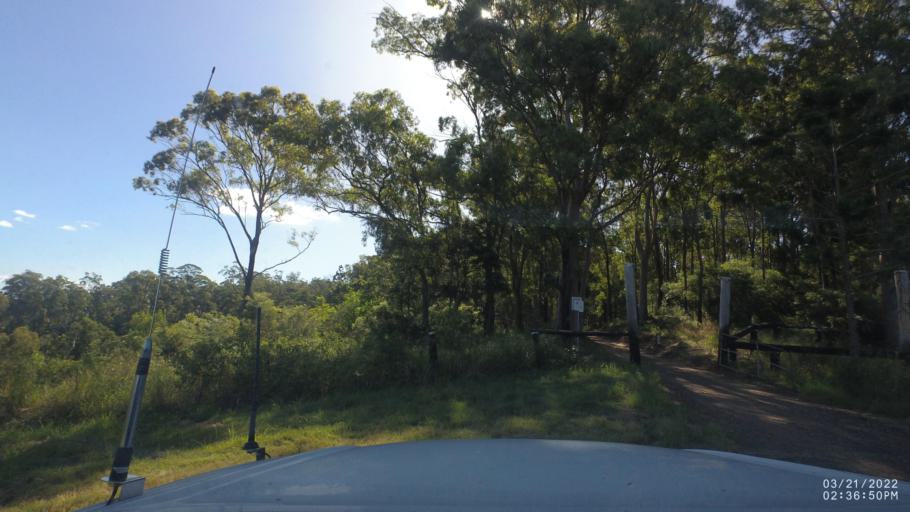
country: AU
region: Queensland
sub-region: Ipswich
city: Deebing Heights
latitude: -27.8246
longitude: 152.8145
